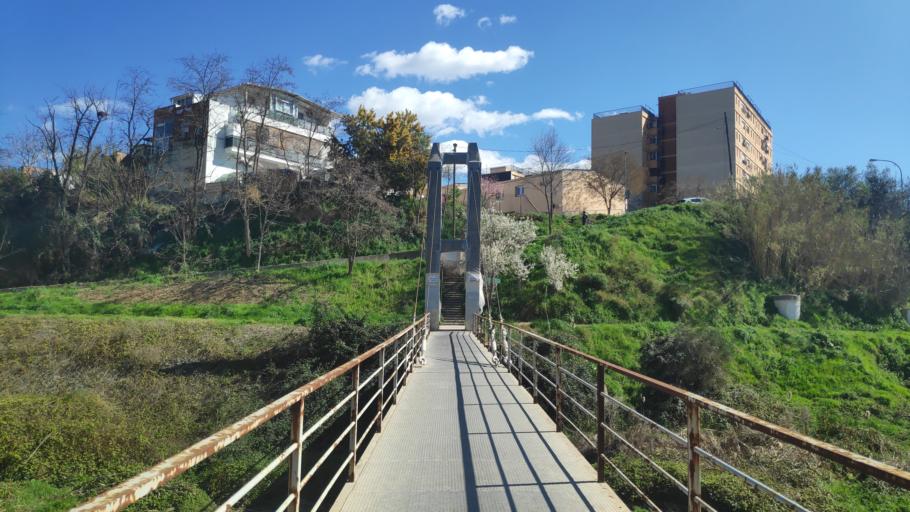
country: ES
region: Catalonia
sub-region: Provincia de Barcelona
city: Sabadell
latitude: 41.5502
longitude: 2.1202
